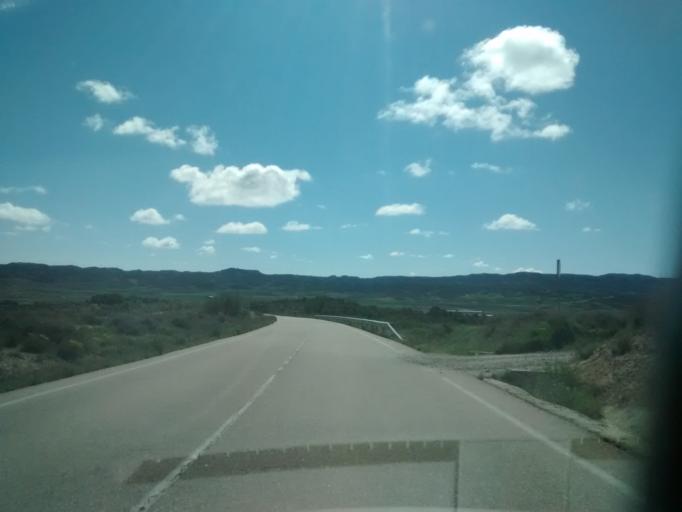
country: ES
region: Aragon
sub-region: Provincia de Zaragoza
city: Lecinena
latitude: 41.7908
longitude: -0.6325
